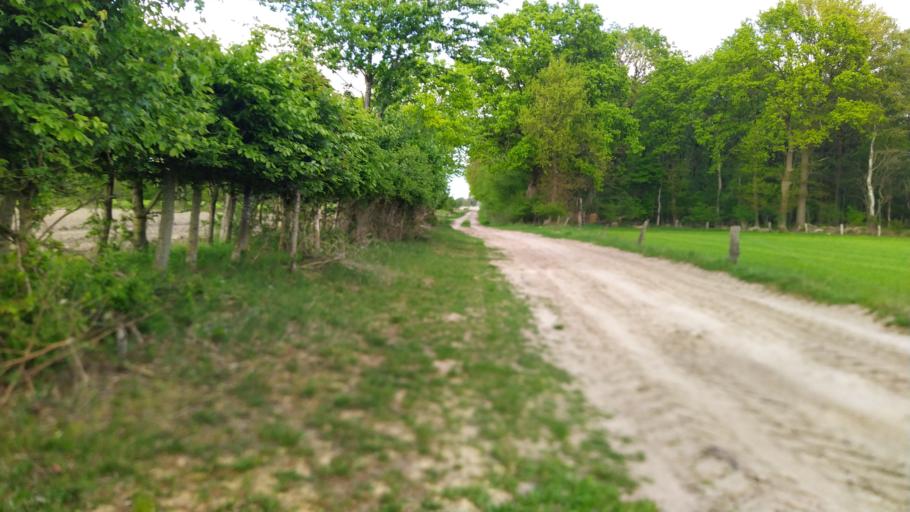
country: DE
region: Lower Saxony
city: Brest
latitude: 53.4134
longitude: 9.3866
